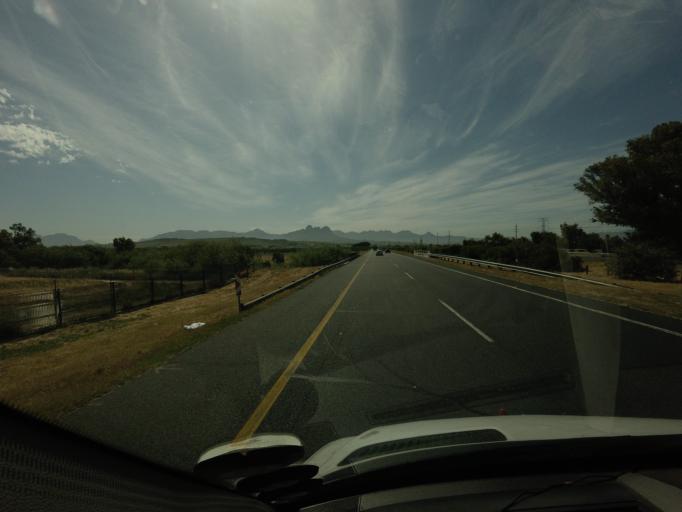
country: ZA
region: Western Cape
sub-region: Cape Winelands District Municipality
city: Stellenbosch
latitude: -34.0429
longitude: 18.7358
